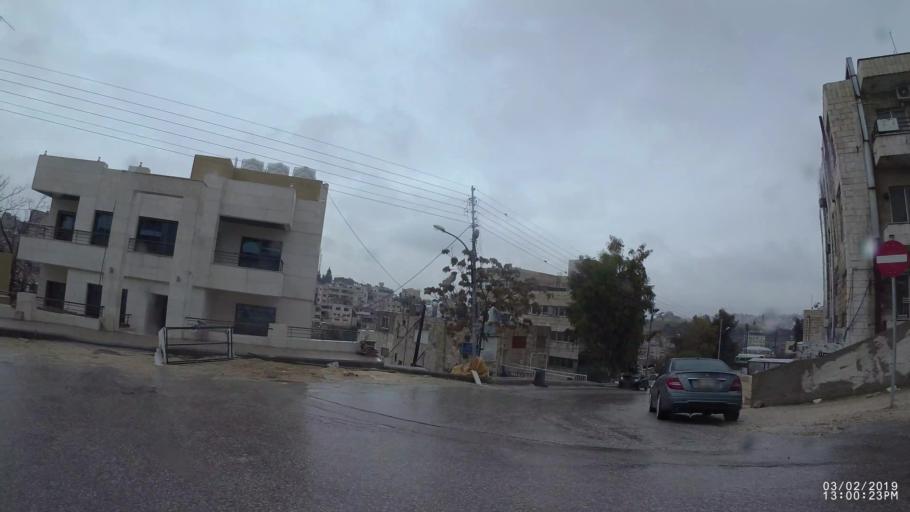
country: JO
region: Amman
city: Amman
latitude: 31.9570
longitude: 35.9284
